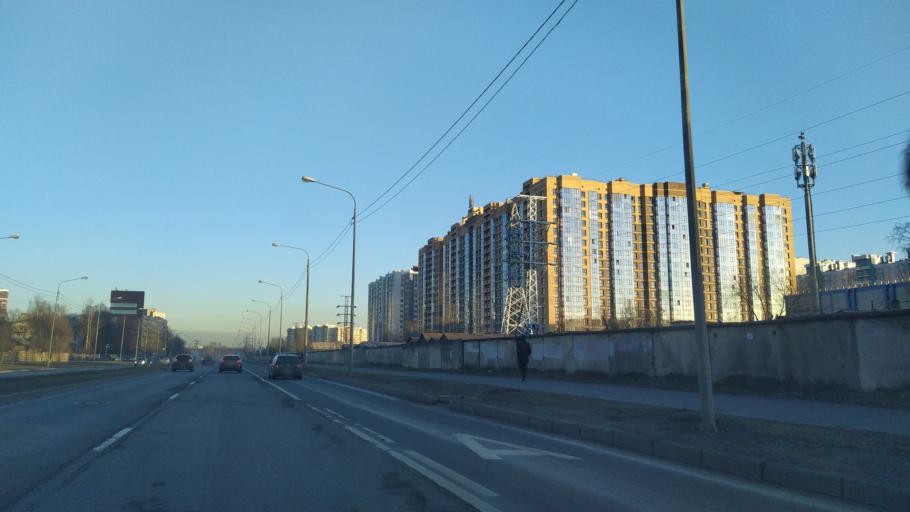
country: RU
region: St.-Petersburg
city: Kushelevka
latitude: 59.9830
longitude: 30.3714
